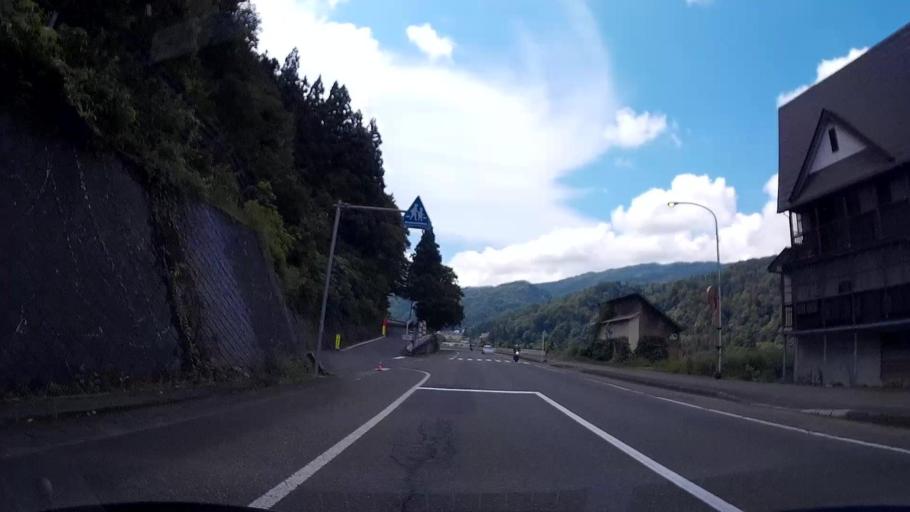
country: JP
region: Niigata
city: Tokamachi
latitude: 36.9955
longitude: 138.6020
